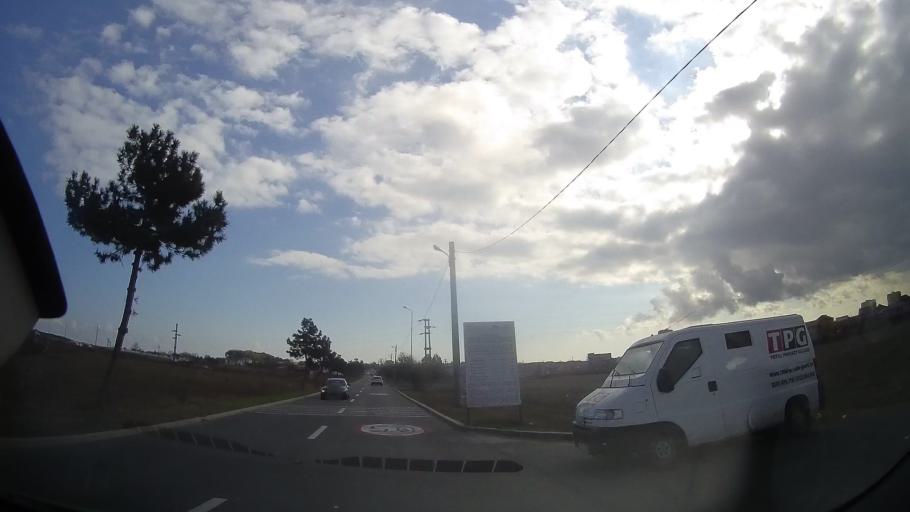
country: RO
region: Constanta
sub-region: Oras Techirghiol
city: Techirghiol
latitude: 44.0650
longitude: 28.5939
